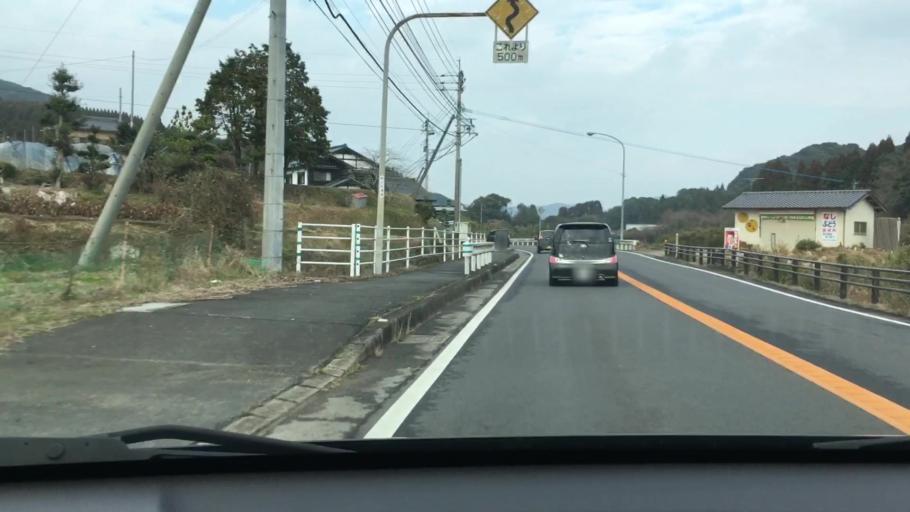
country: JP
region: Saga Prefecture
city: Imaricho-ko
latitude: 33.3177
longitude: 129.9290
